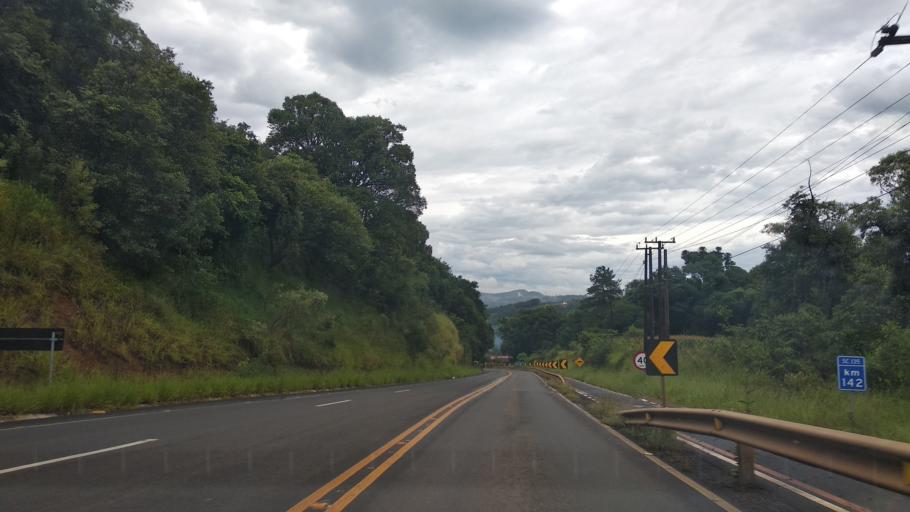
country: BR
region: Santa Catarina
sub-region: Videira
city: Videira
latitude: -27.0890
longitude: -51.2426
